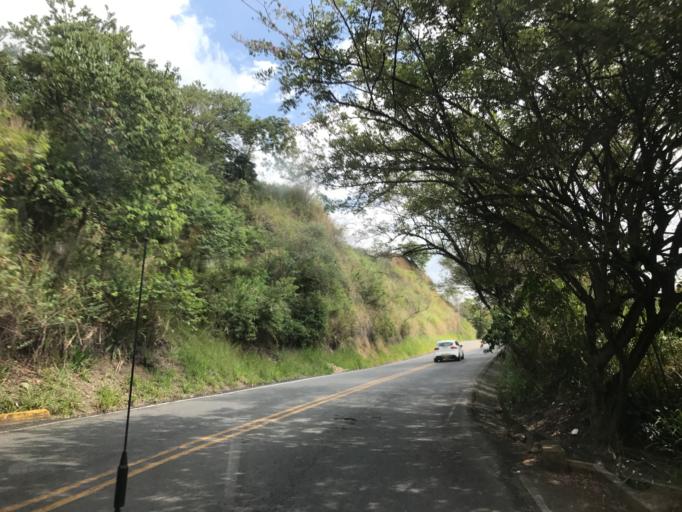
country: CO
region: Valle del Cauca
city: Cartago
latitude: 4.7327
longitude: -75.8945
